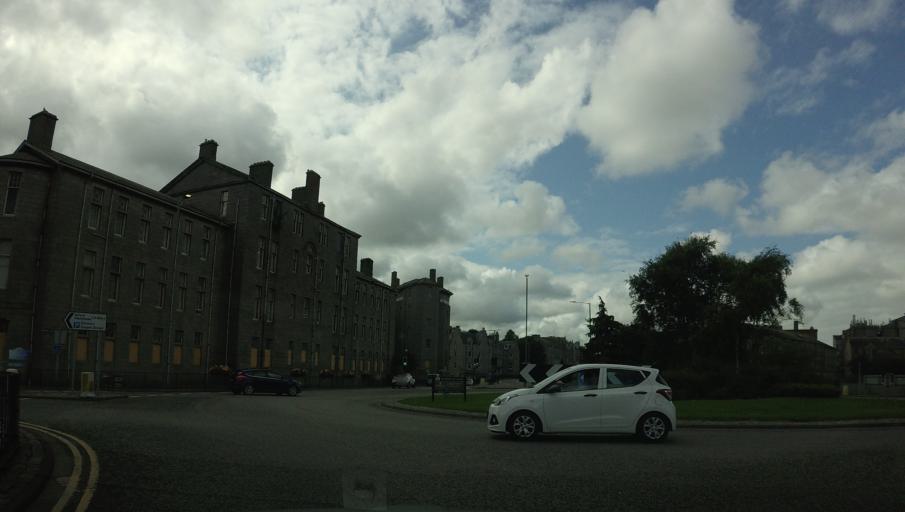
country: GB
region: Scotland
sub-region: Aberdeen City
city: Aberdeen
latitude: 57.1494
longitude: -2.1050
